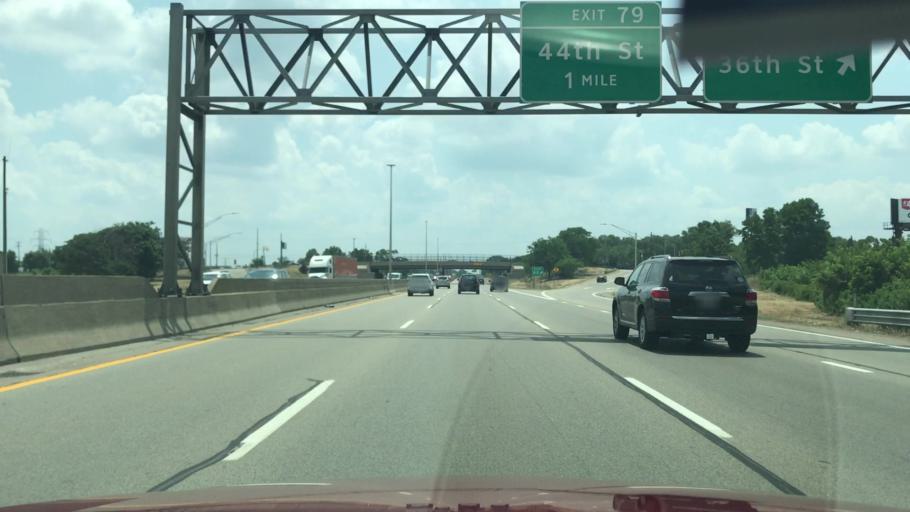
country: US
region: Michigan
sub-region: Kent County
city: Wyoming
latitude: 42.9012
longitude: -85.6777
